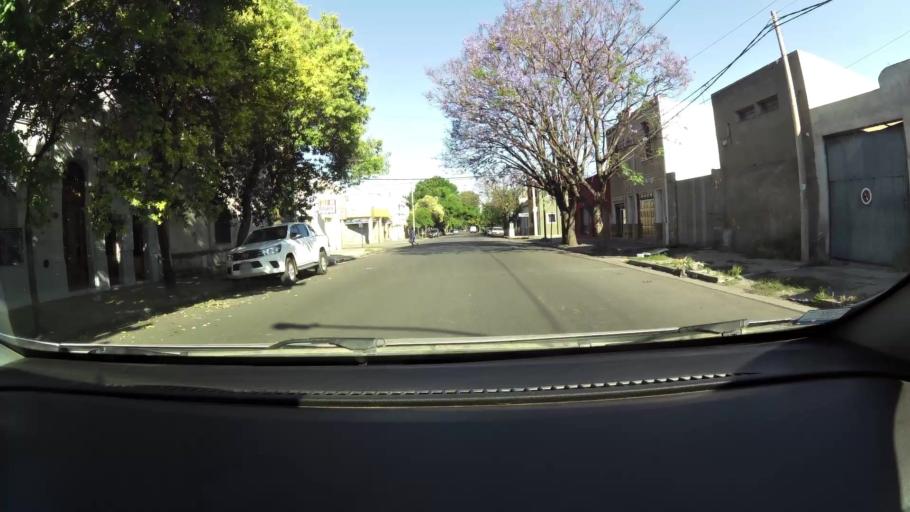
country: AR
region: Cordoba
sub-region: Departamento de Capital
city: Cordoba
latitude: -31.3979
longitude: -64.1744
